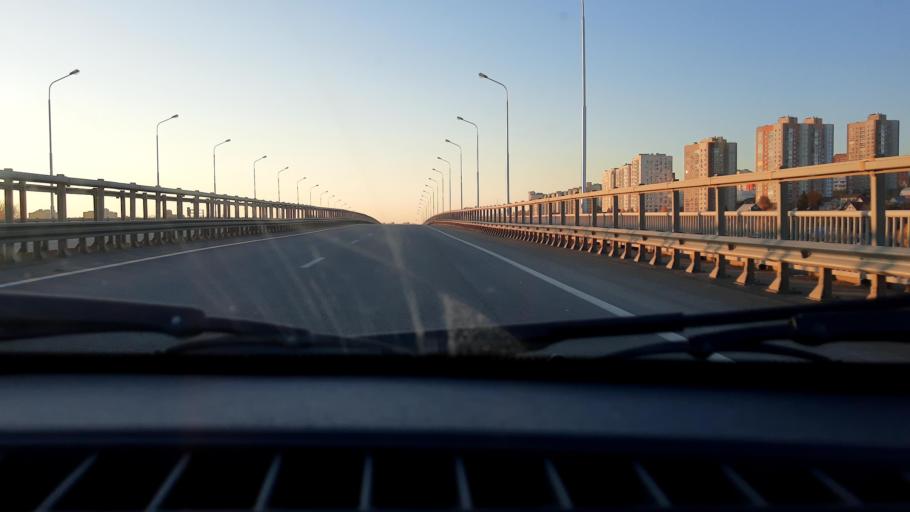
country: RU
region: Bashkortostan
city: Ufa
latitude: 54.6831
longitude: 56.0019
